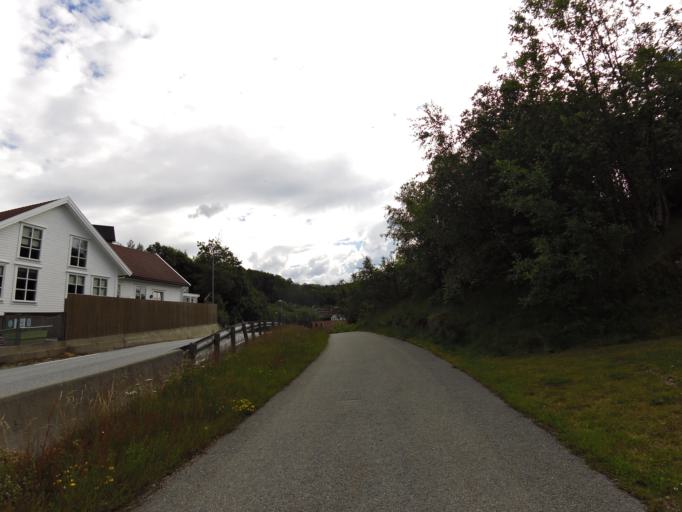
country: NO
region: Vest-Agder
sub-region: Lindesnes
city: Vigeland
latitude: 58.0511
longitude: 7.1942
